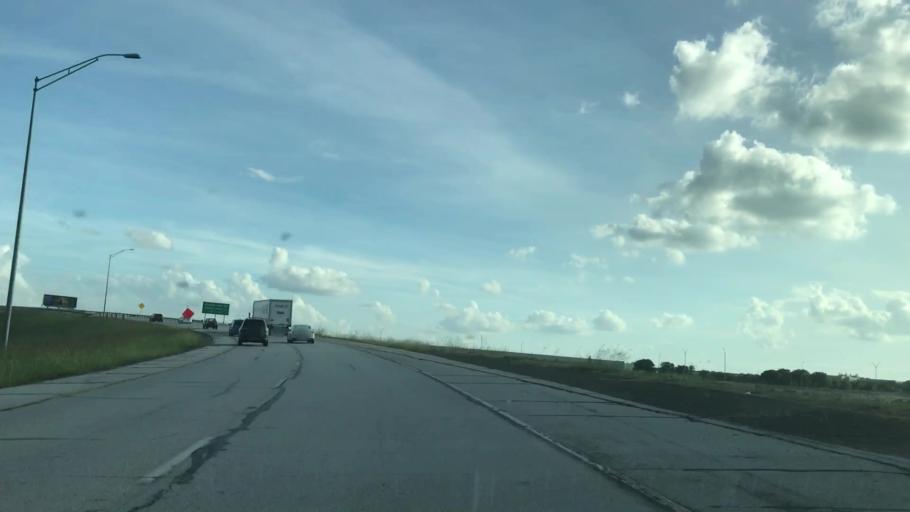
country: US
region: Texas
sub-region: Tarrant County
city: Euless
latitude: 32.8400
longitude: -97.0421
